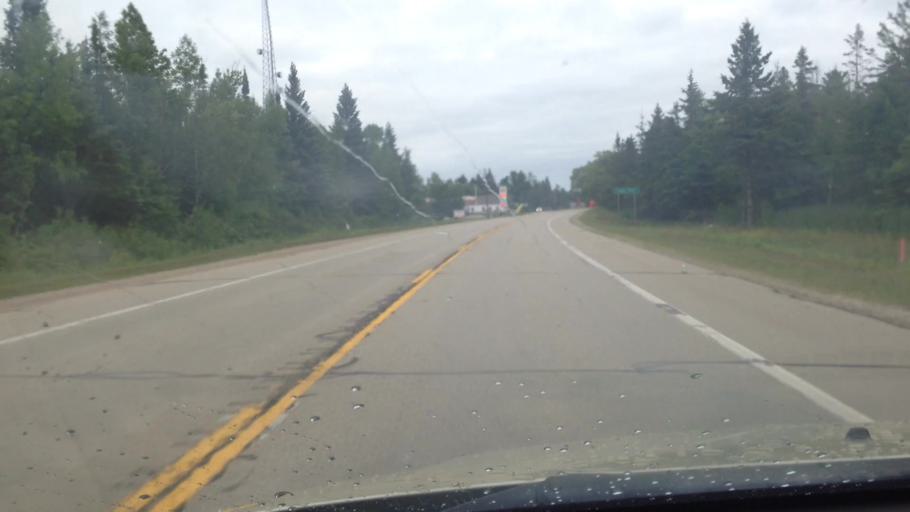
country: US
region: Michigan
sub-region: Menominee County
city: Menominee
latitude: 45.4074
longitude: -87.3594
